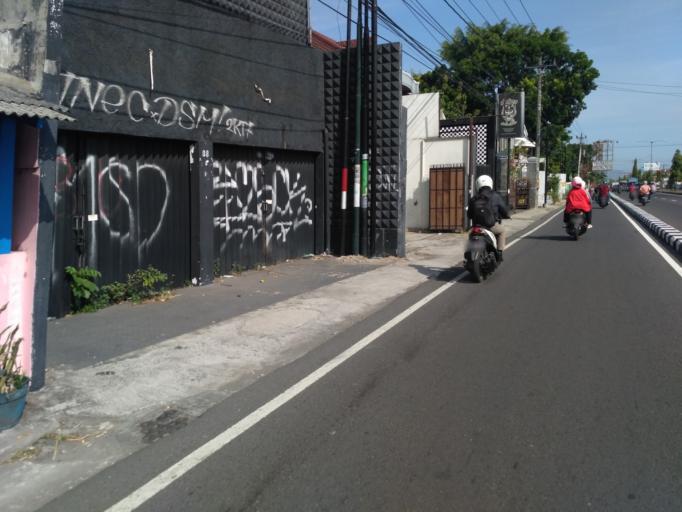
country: ID
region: Daerah Istimewa Yogyakarta
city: Depok
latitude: -7.7719
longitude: 110.4310
